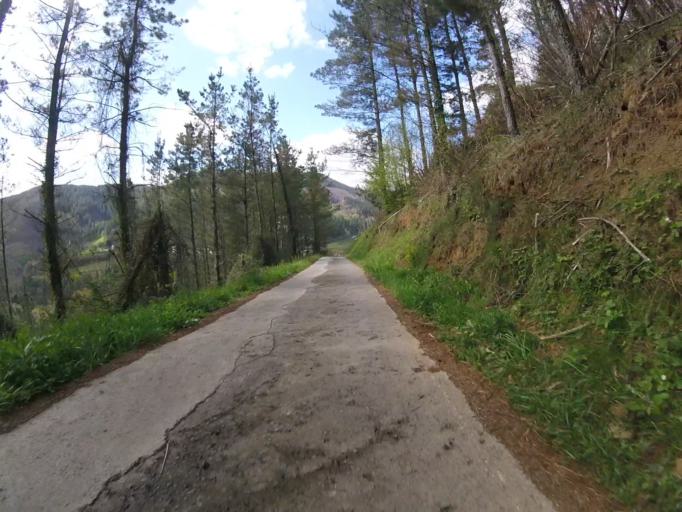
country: ES
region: Basque Country
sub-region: Provincia de Guipuzcoa
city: Albiztur
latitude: 43.1315
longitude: -2.1243
